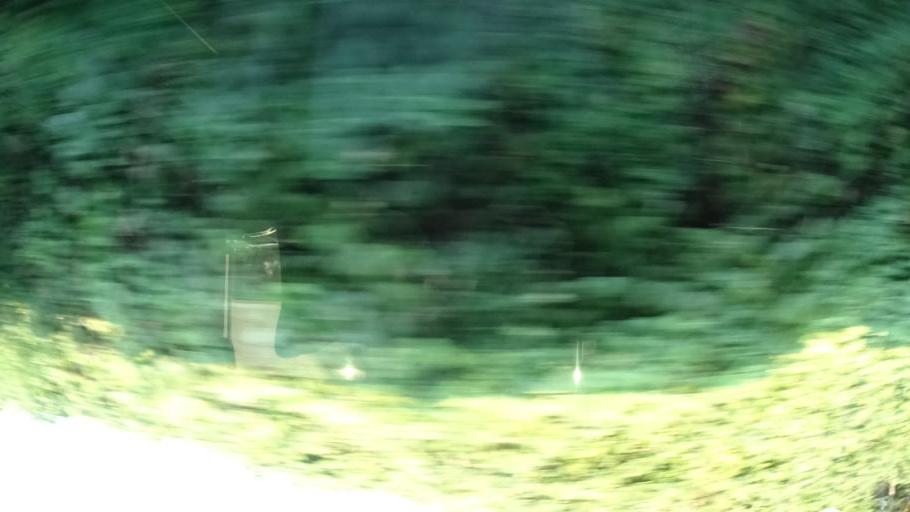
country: JP
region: Ibaraki
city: Naka
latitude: 36.0471
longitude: 140.1783
